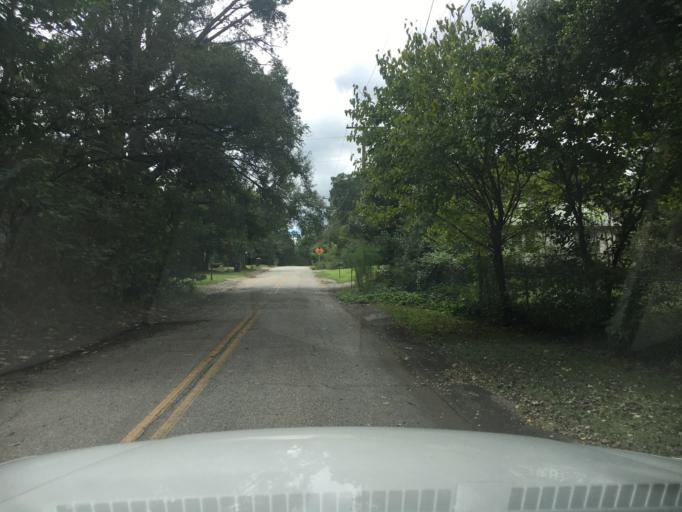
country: US
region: South Carolina
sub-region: Spartanburg County
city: Duncan
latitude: 34.9406
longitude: -82.1476
